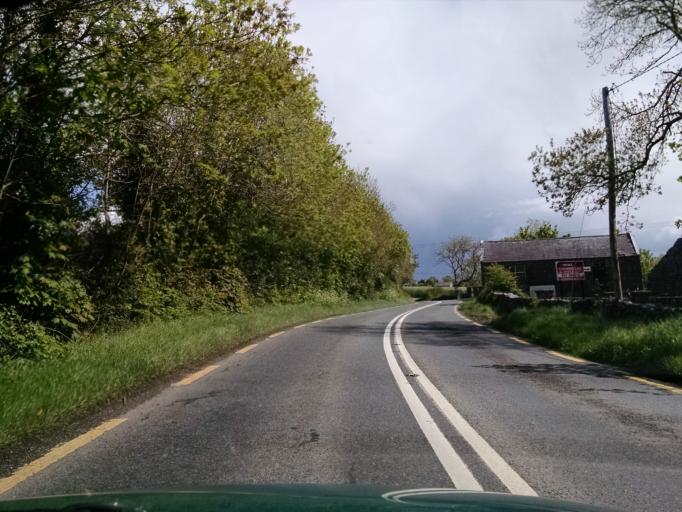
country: IE
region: Connaught
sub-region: County Galway
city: Oranmore
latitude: 53.2040
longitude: -8.8749
